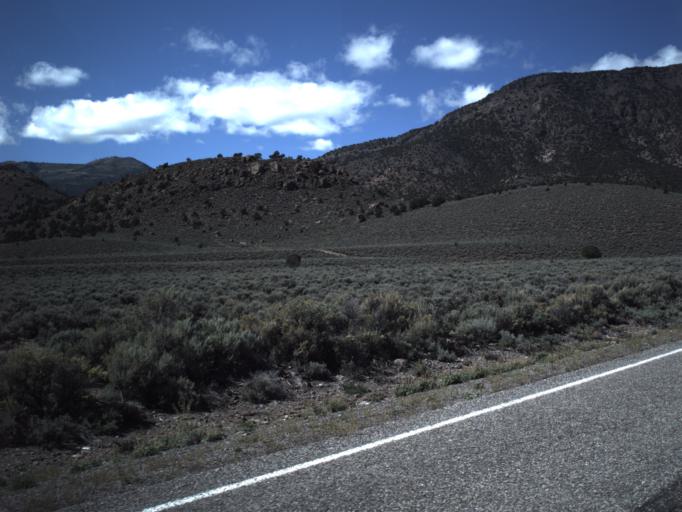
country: US
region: Utah
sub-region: Piute County
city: Junction
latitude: 38.2580
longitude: -112.2464
